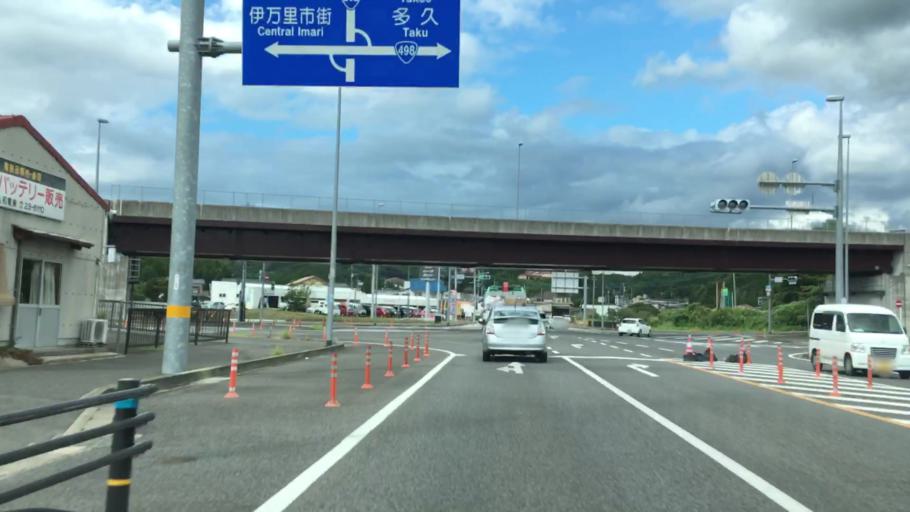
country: JP
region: Saga Prefecture
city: Imaricho-ko
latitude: 33.2811
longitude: 129.8964
